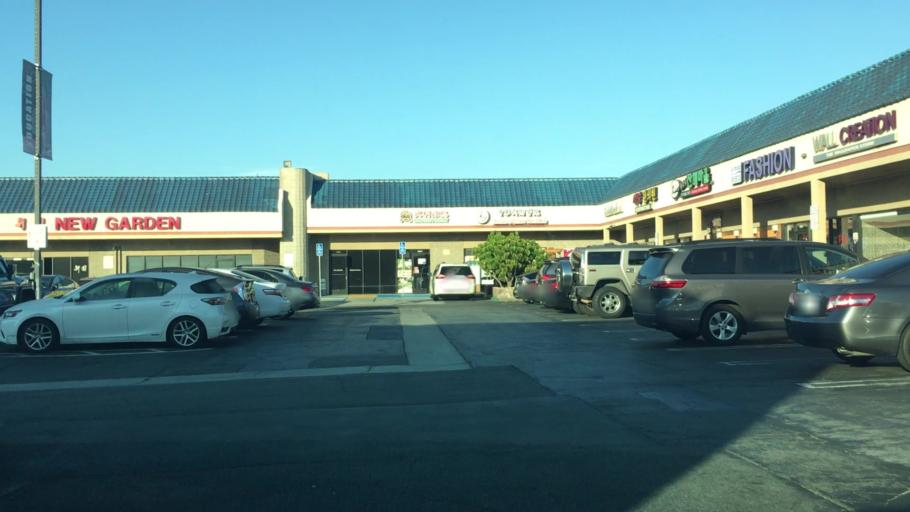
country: US
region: California
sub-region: Los Angeles County
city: Rowland Heights
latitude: 33.9871
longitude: -117.8955
